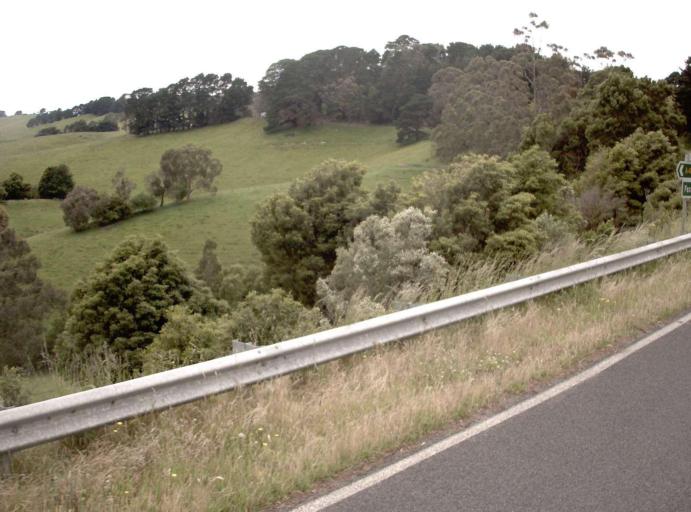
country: AU
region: Victoria
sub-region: Latrobe
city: Moe
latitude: -38.6191
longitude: 146.1466
